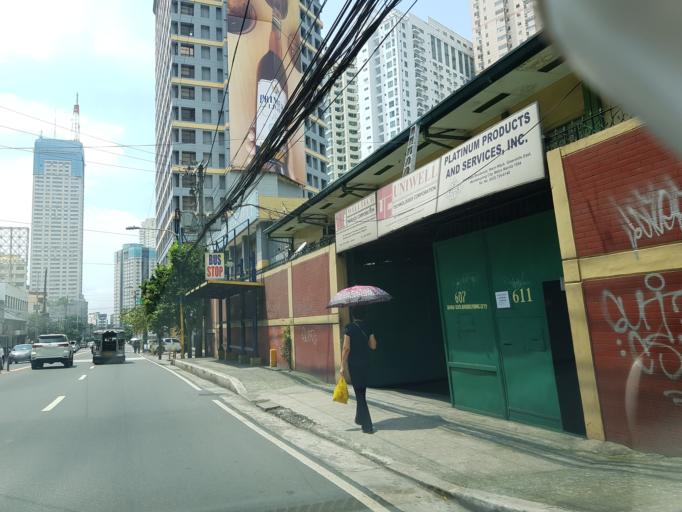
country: PH
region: Metro Manila
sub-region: Mandaluyong
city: Mandaluyong City
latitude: 14.5845
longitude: 121.0498
